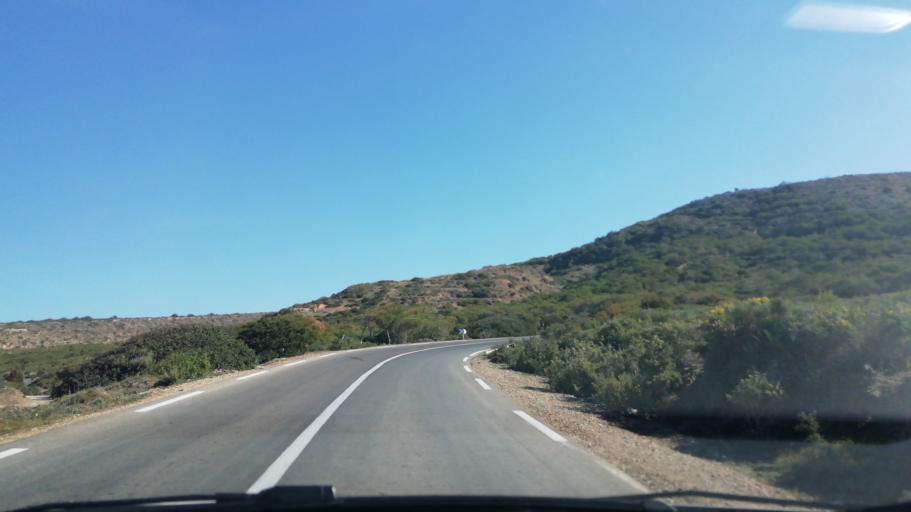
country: DZ
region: Ain Temouchent
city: El Amria
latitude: 35.6446
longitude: -1.0546
